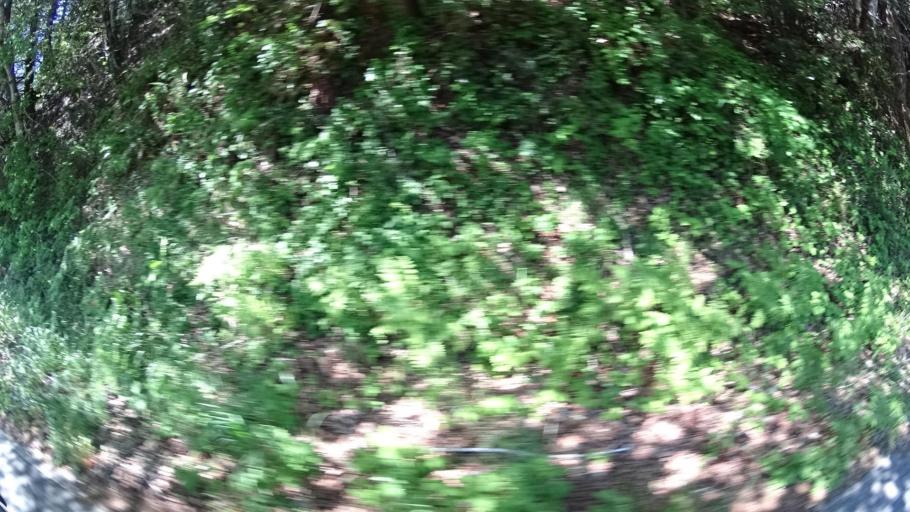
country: US
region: California
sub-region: Humboldt County
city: Rio Dell
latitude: 40.2662
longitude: -124.1976
